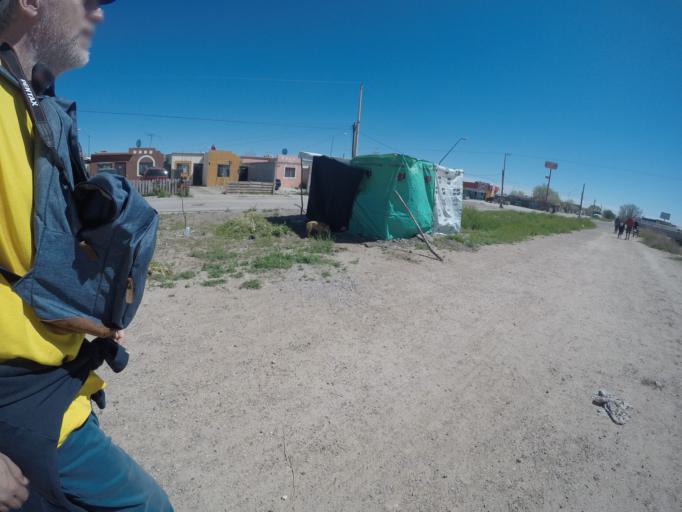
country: US
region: Texas
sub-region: El Paso County
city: Socorro Mission Number 1 Colonia
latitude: 31.6044
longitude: -106.3097
